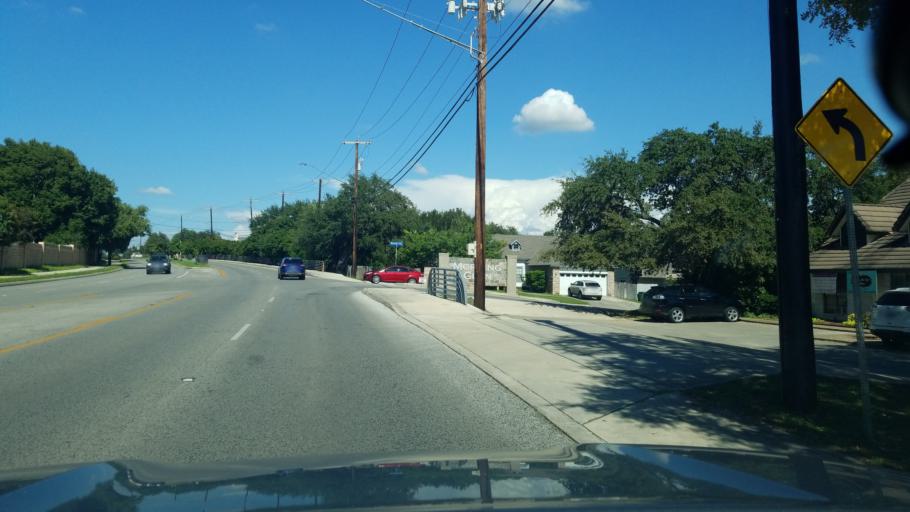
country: US
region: Texas
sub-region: Bexar County
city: Hollywood Park
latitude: 29.5802
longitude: -98.4397
